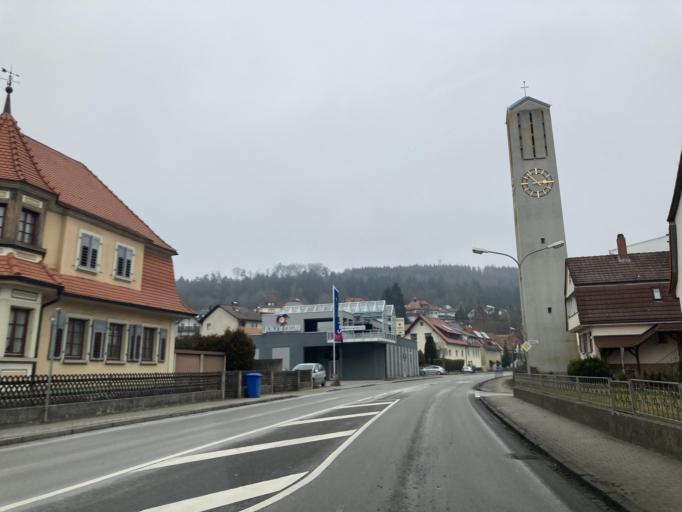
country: DE
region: Baden-Wuerttemberg
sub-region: Freiburg Region
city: Immendingen
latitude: 47.9386
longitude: 8.7356
